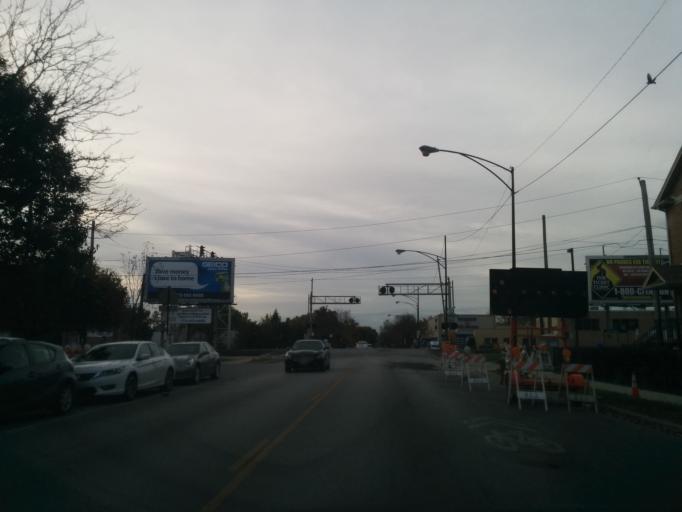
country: US
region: Illinois
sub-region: Cook County
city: Elmwood Park
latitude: 41.9171
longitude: -87.7852
